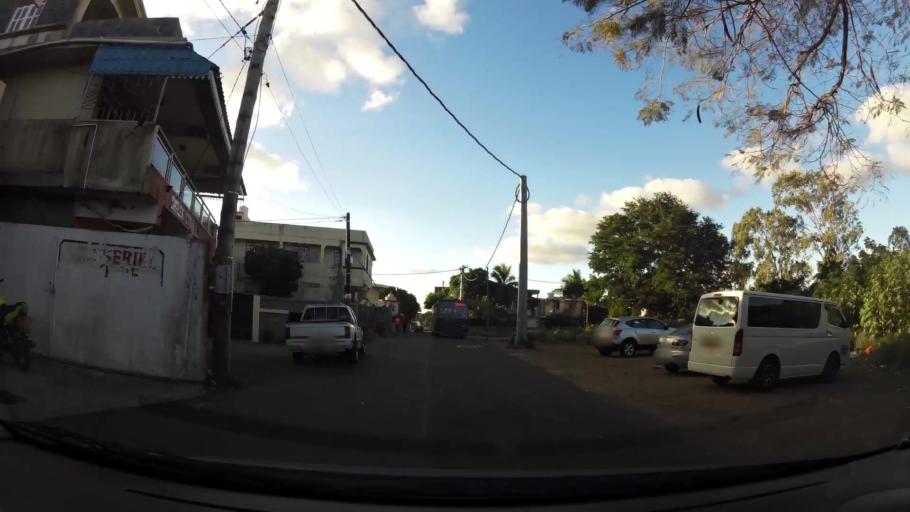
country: MU
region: Plaines Wilhems
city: Quatre Bornes
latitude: -20.2468
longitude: 57.4618
